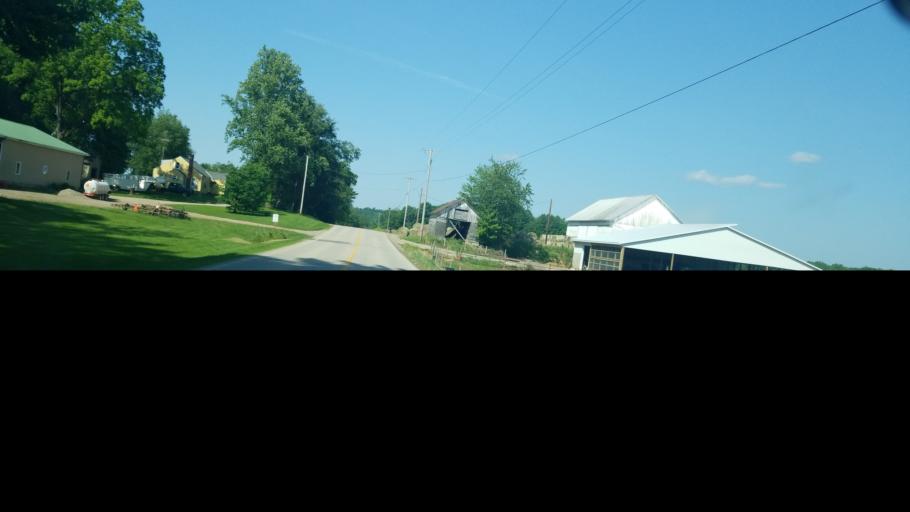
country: US
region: Ohio
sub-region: Ashland County
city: Loudonville
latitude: 40.6738
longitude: -82.2977
